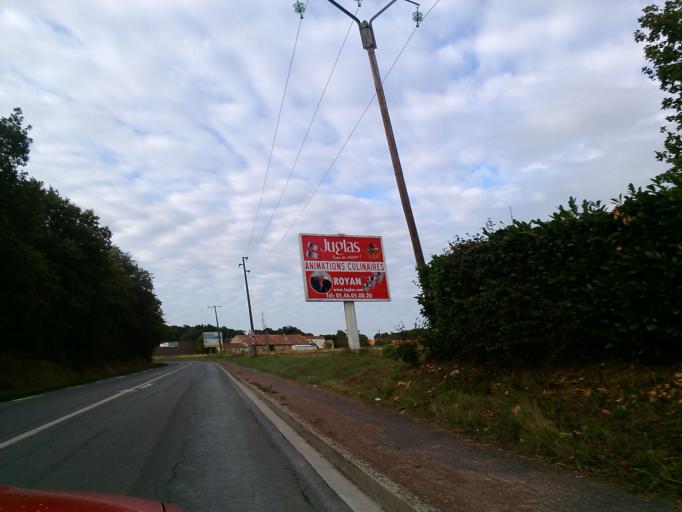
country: FR
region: Poitou-Charentes
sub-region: Departement de la Charente-Maritime
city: Saint-Sulpice-de-Royan
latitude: 45.6510
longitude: -1.0241
